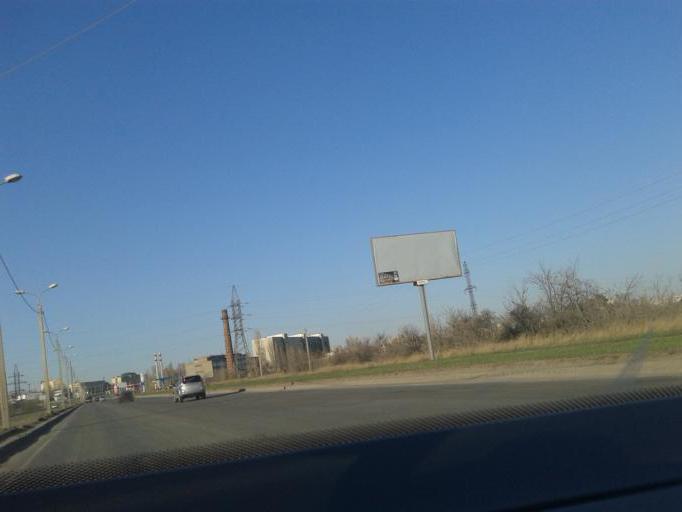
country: RU
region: Volgograd
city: Volgograd
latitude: 48.7428
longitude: 44.4635
